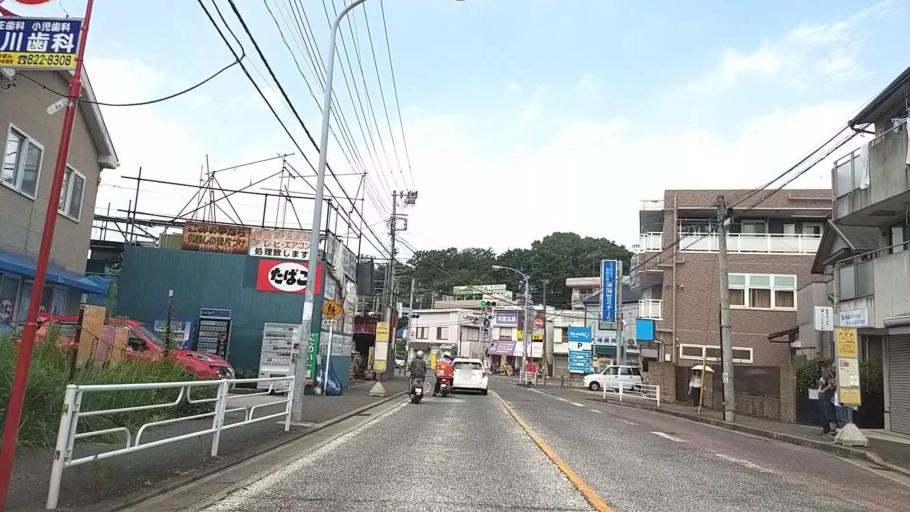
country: JP
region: Kanagawa
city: Yokohama
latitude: 35.4159
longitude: 139.5749
